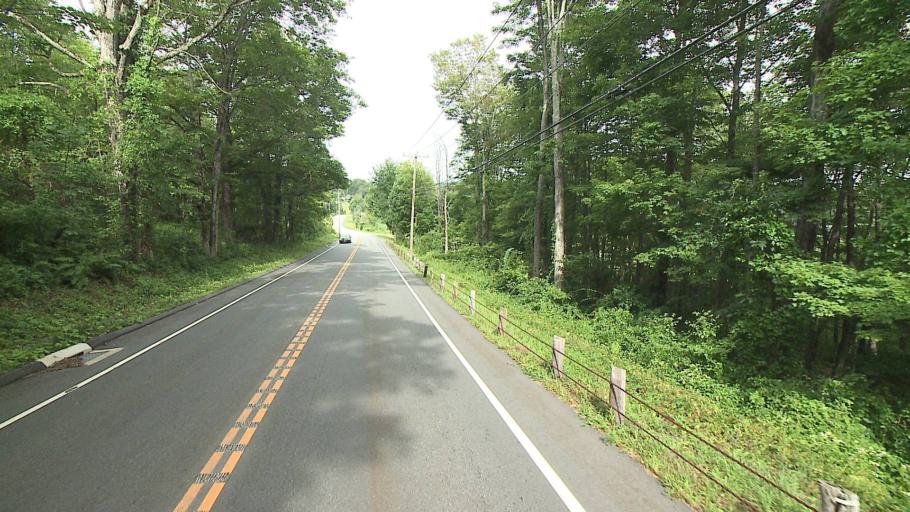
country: US
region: Connecticut
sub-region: Litchfield County
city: New Preston
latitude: 41.7154
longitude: -73.3226
